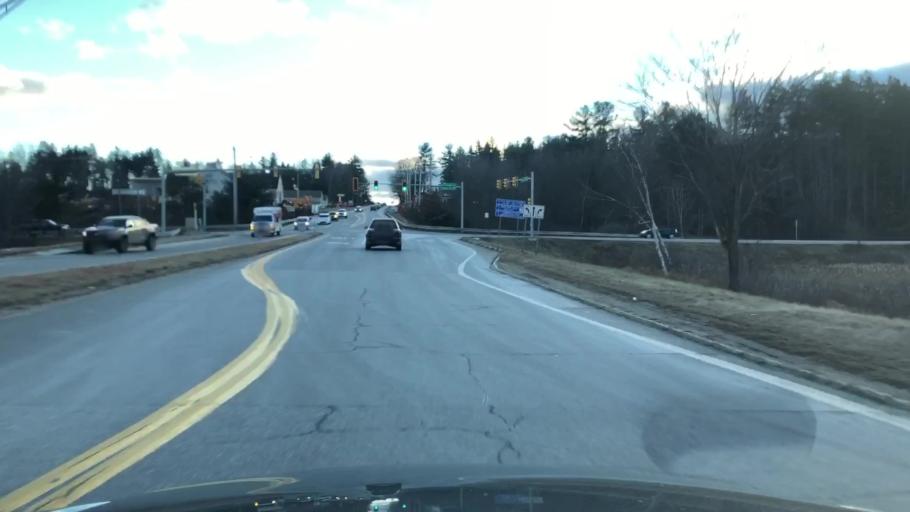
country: US
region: New Hampshire
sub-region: Hillsborough County
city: Milford
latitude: 42.8163
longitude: -71.6464
